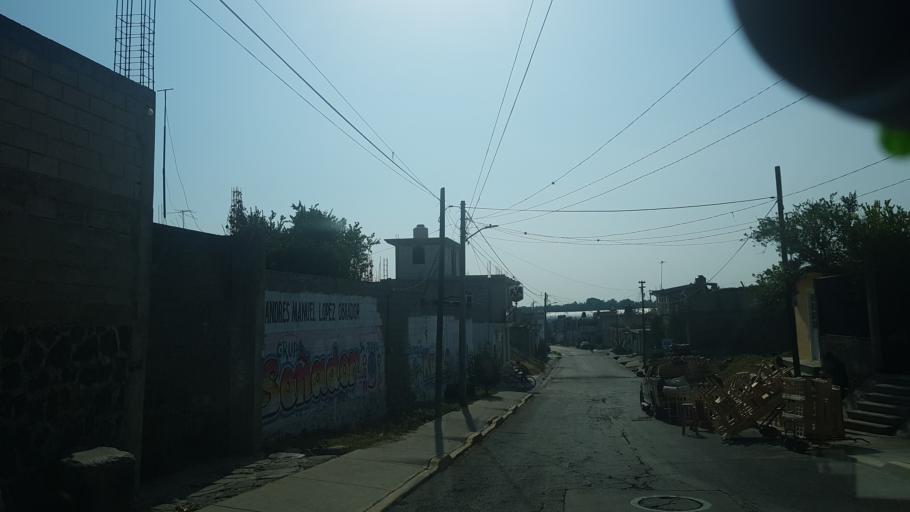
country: MX
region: Puebla
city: San Nicolas de los Ranchos
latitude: 19.0727
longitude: -98.4836
